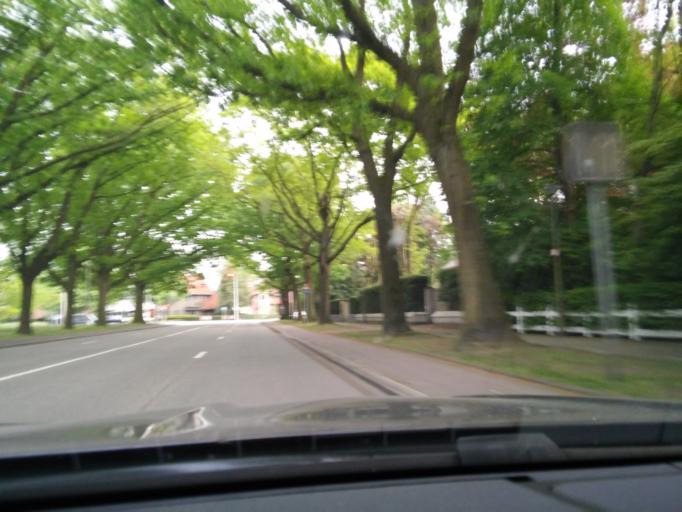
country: BE
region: Flanders
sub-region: Provincie Antwerpen
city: Edegem
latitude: 51.1769
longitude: 4.4115
